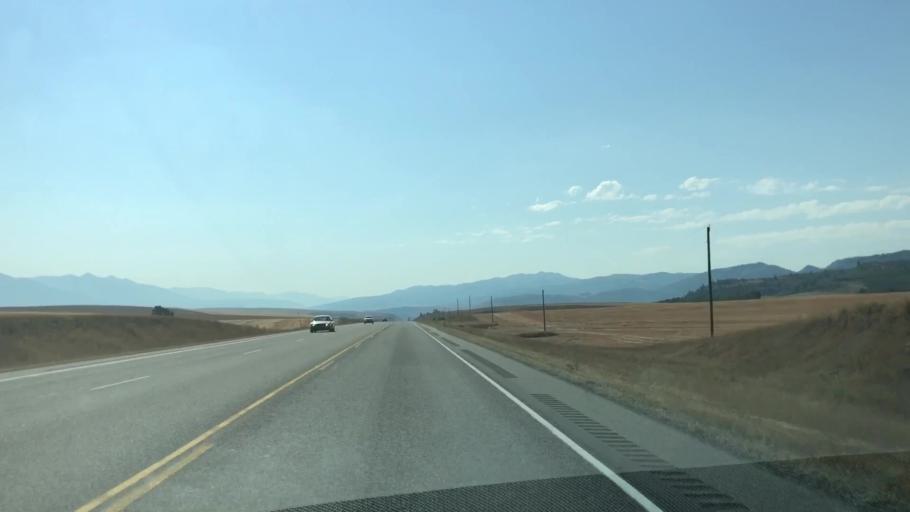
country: US
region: Idaho
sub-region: Teton County
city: Victor
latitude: 43.5023
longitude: -111.4677
